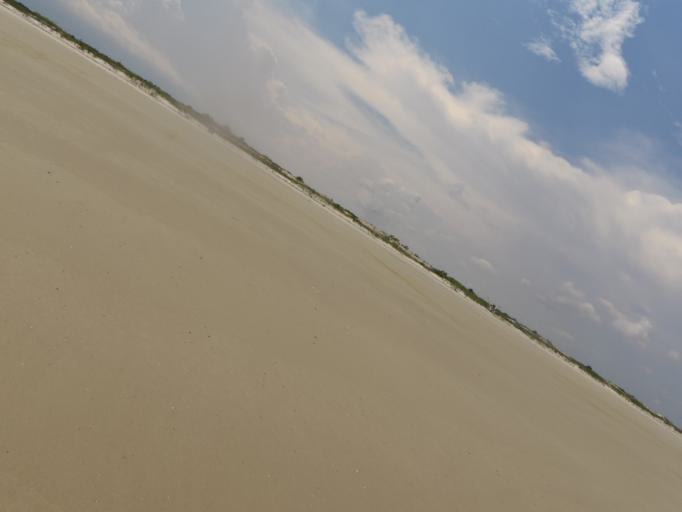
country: US
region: Florida
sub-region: Duval County
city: Atlantic Beach
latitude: 30.4386
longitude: -81.4072
